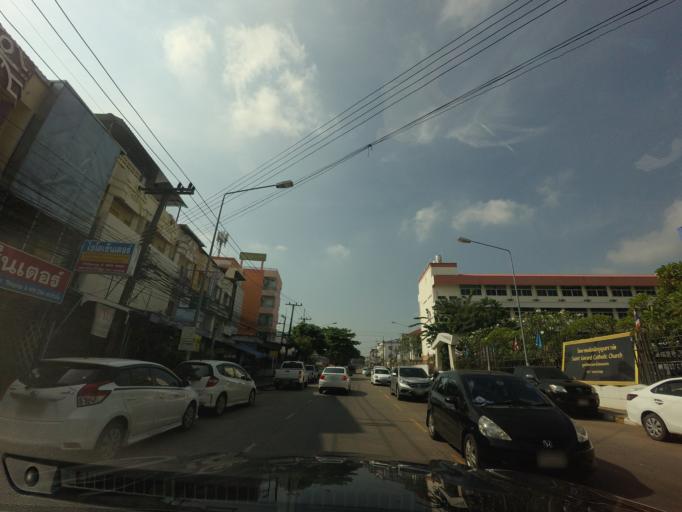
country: TH
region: Khon Kaen
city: Khon Kaen
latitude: 16.4279
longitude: 102.8513
